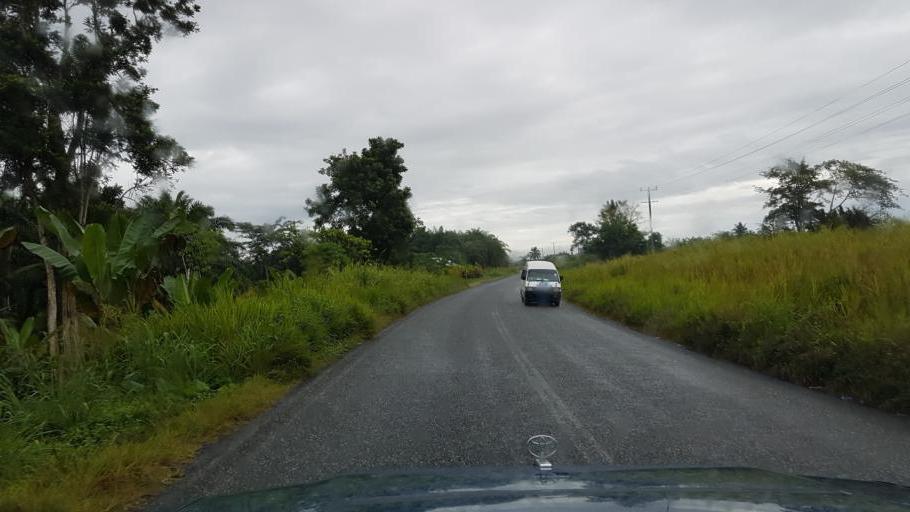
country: PG
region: Northern Province
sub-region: Sohe
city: Popondetta
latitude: -8.7772
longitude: 148.2094
